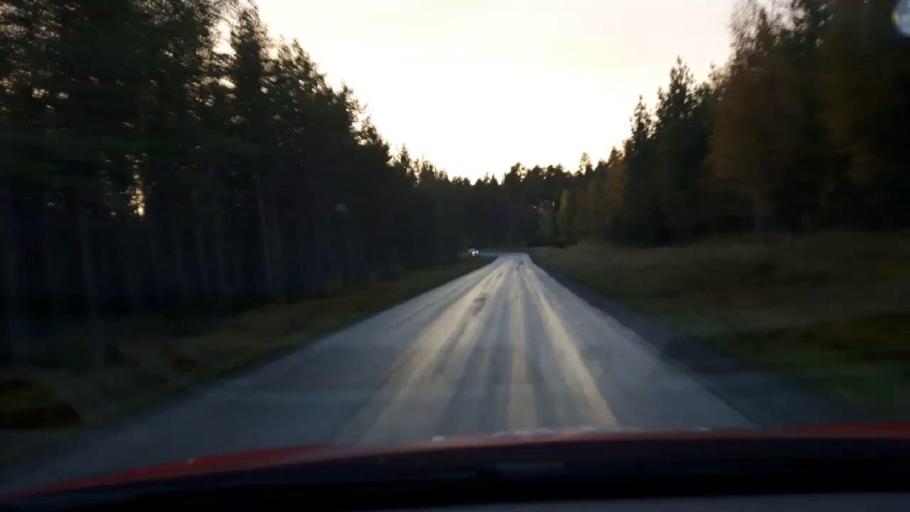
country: SE
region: Jaemtland
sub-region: OEstersunds Kommun
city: Lit
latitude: 63.2909
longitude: 14.8203
